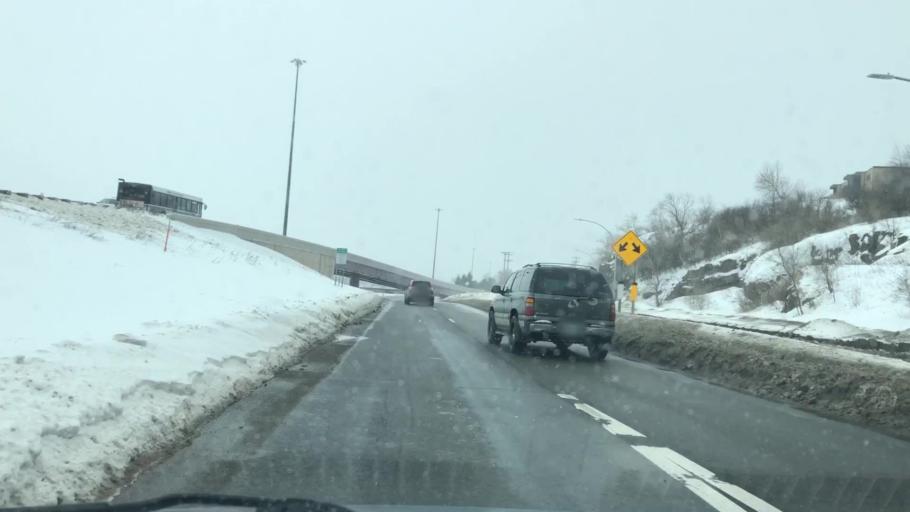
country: US
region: Minnesota
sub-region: Saint Louis County
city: Duluth
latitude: 46.7777
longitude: -92.1092
